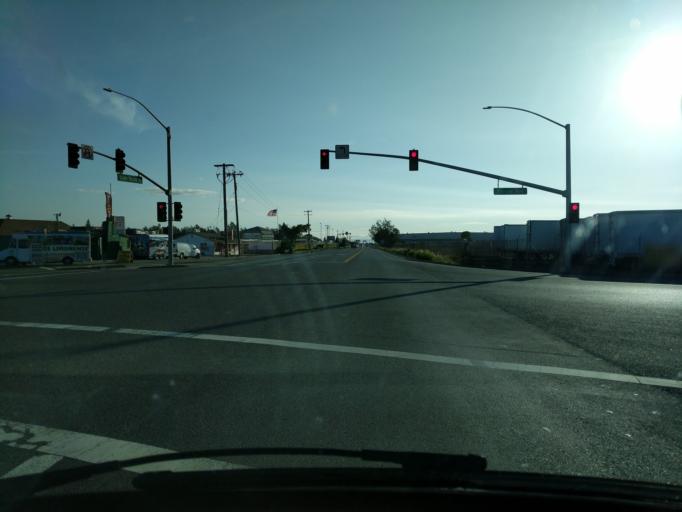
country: US
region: California
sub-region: San Joaquin County
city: Stockton
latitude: 37.9330
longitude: -121.3120
